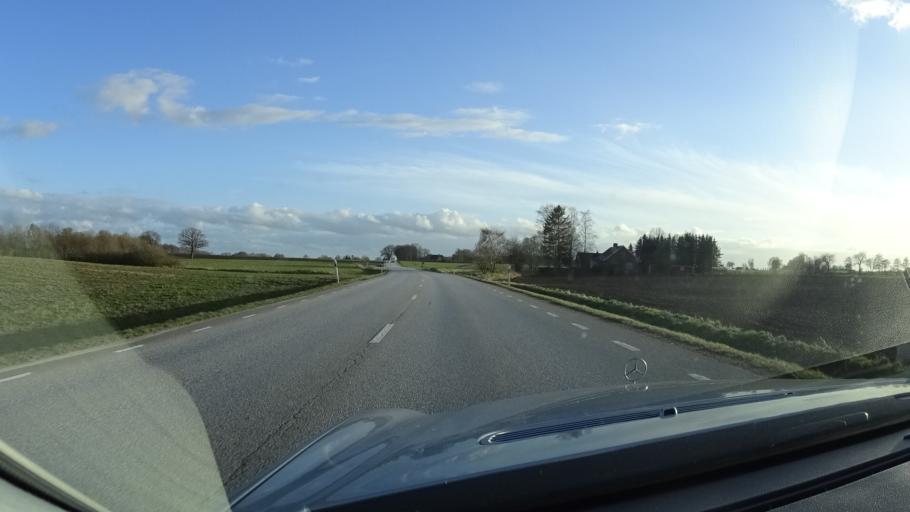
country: SE
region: Skane
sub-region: Hoors Kommun
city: Loberod
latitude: 55.8298
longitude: 13.4902
